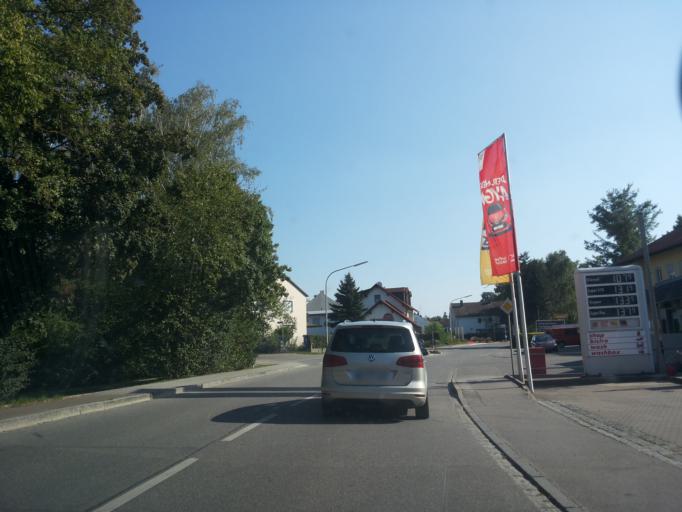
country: DE
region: Bavaria
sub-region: Lower Bavaria
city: Neustadt an der Donau
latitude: 48.8231
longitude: 11.7819
